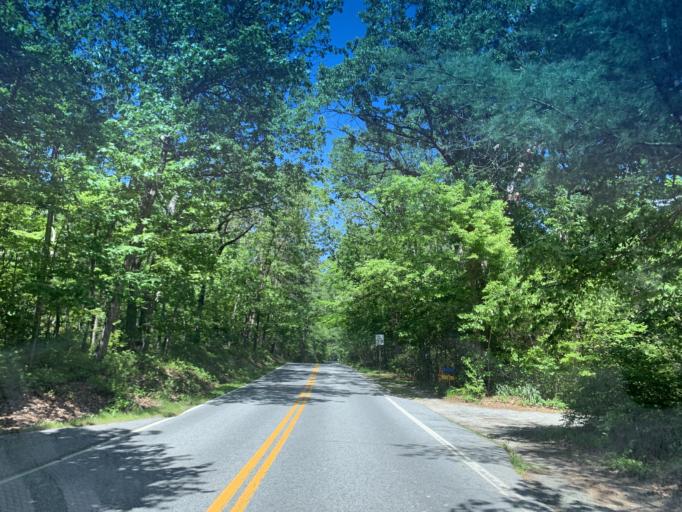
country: US
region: Maryland
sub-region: Cecil County
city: North East
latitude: 39.5558
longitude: -75.8986
